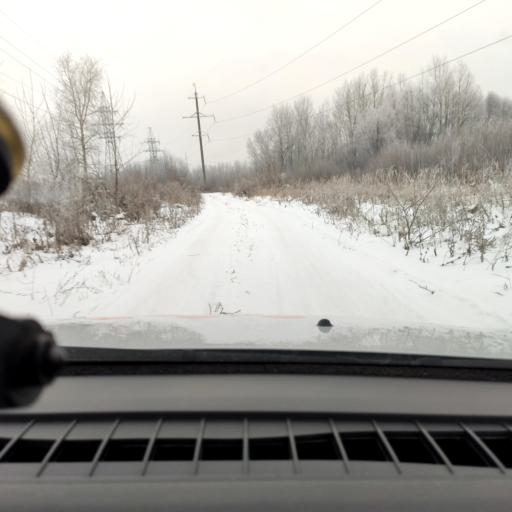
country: RU
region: Samara
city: Samara
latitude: 53.1434
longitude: 50.1882
